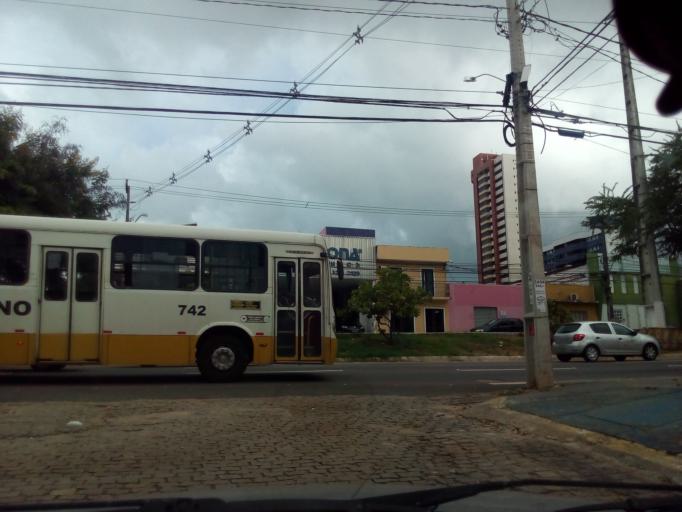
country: BR
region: Rio Grande do Norte
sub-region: Natal
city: Natal
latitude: -5.7996
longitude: -35.2059
